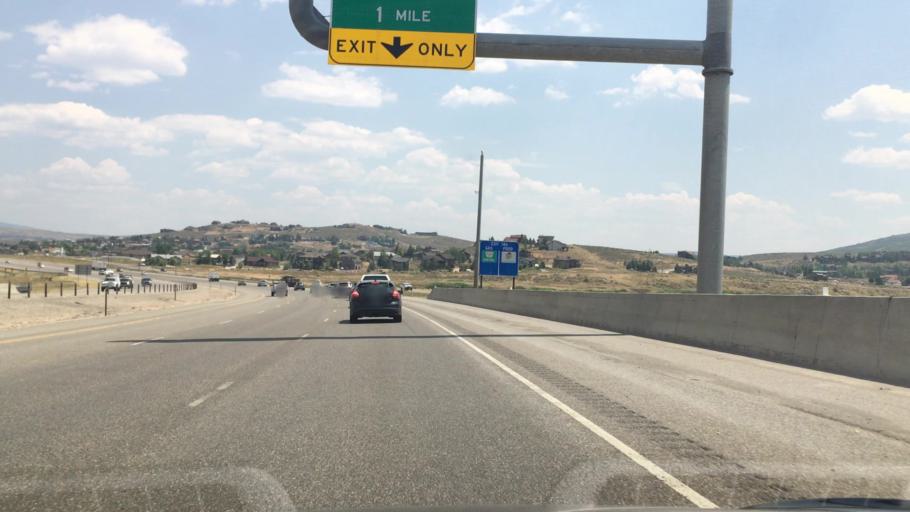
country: US
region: Utah
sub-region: Summit County
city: Snyderville
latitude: 40.7213
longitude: -111.5231
